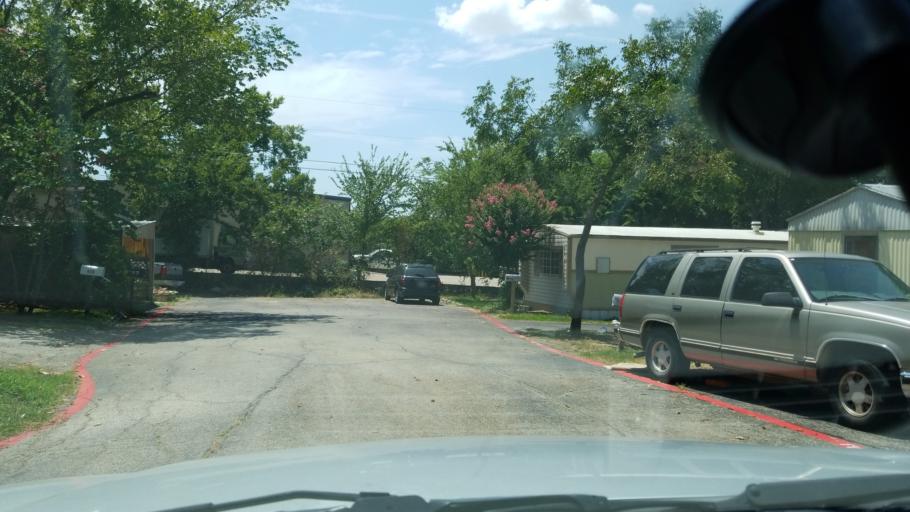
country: US
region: Texas
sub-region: Dallas County
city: Irving
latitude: 32.8190
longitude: -96.9952
